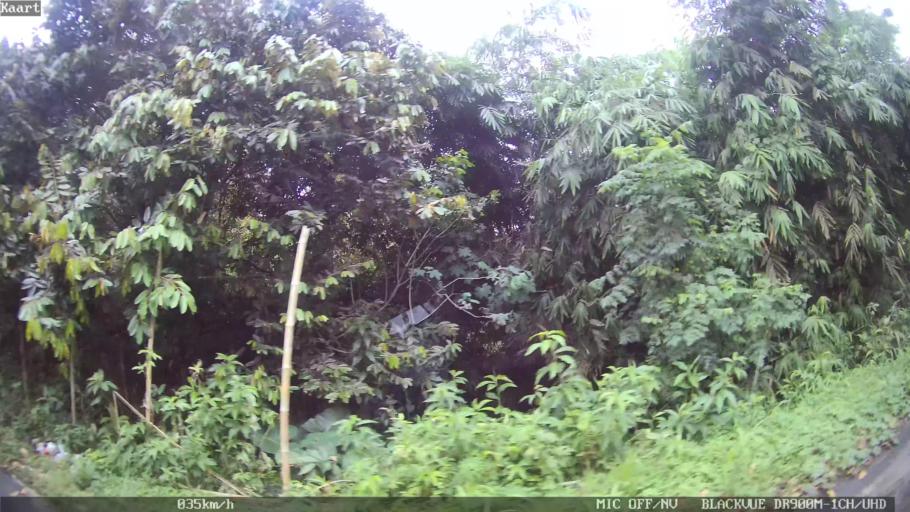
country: ID
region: Lampung
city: Bandarlampung
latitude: -5.4278
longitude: 105.1993
